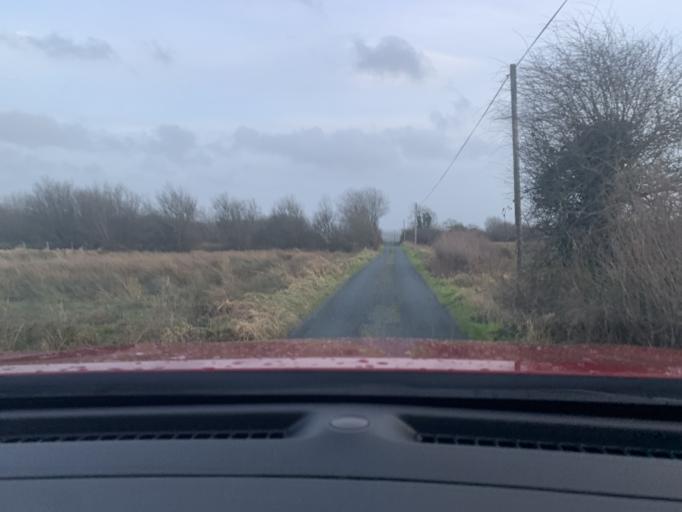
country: IE
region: Connaught
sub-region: Roscommon
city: Ballaghaderreen
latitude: 53.9457
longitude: -8.5029
